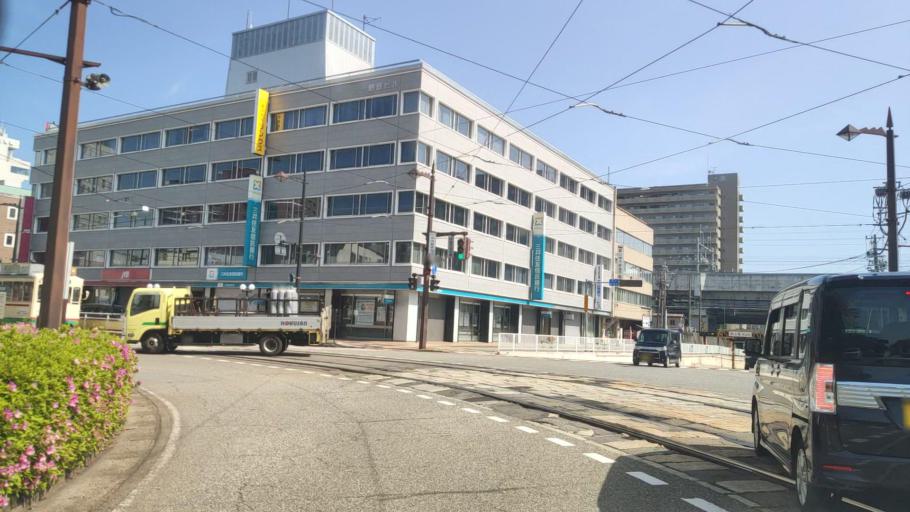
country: JP
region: Toyama
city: Toyama-shi
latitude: 36.6989
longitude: 137.2162
